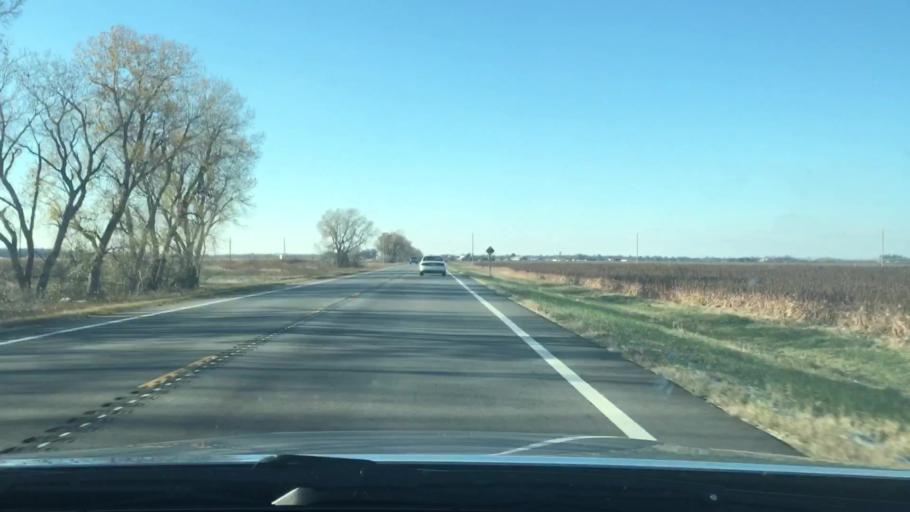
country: US
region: Kansas
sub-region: Reno County
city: Nickerson
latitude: 38.1282
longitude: -98.0557
